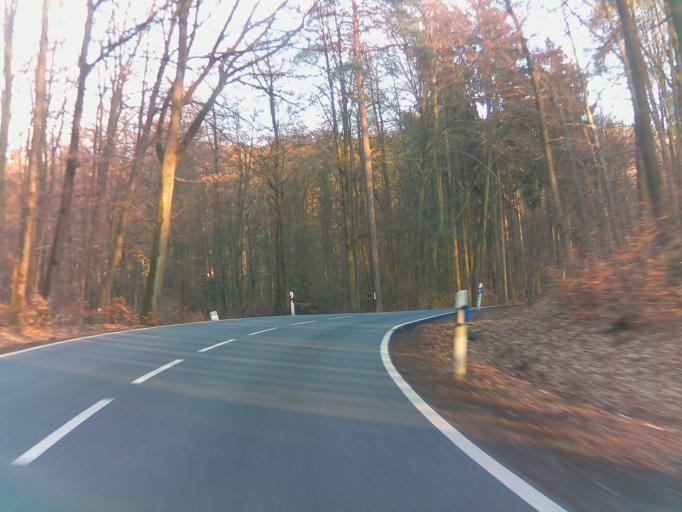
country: DE
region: Bavaria
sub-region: Regierungsbezirk Unterfranken
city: Geiselbach
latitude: 50.1520
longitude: 9.2118
